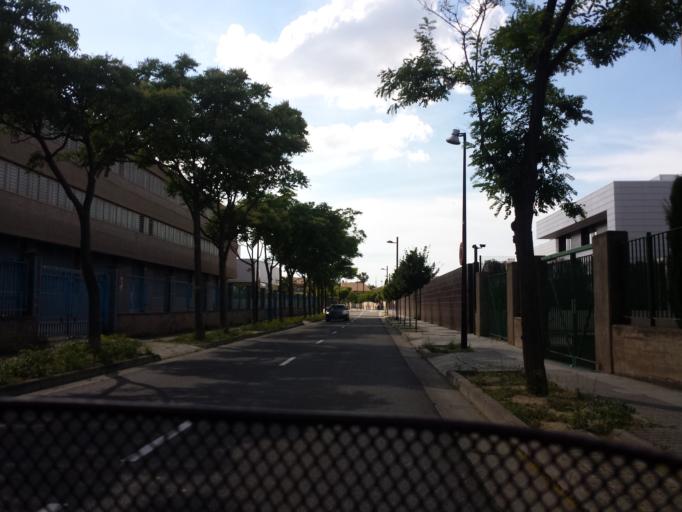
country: ES
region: Aragon
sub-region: Provincia de Zaragoza
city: Delicias
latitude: 41.6284
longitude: -0.9121
